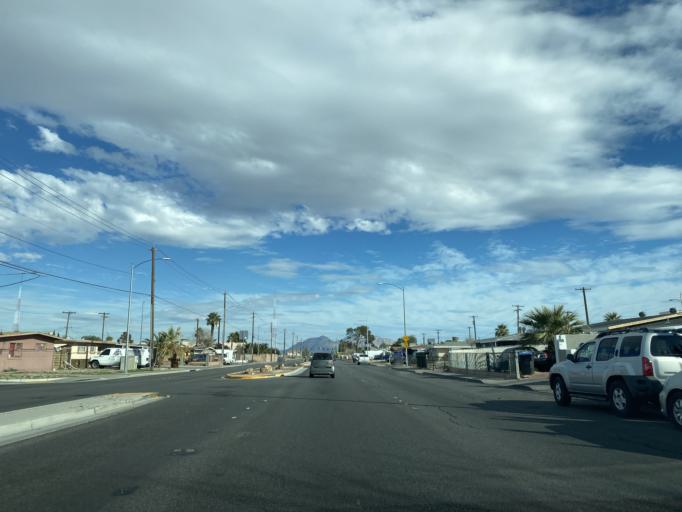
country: US
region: Nevada
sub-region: Clark County
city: Las Vegas
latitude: 36.1885
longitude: -115.1837
